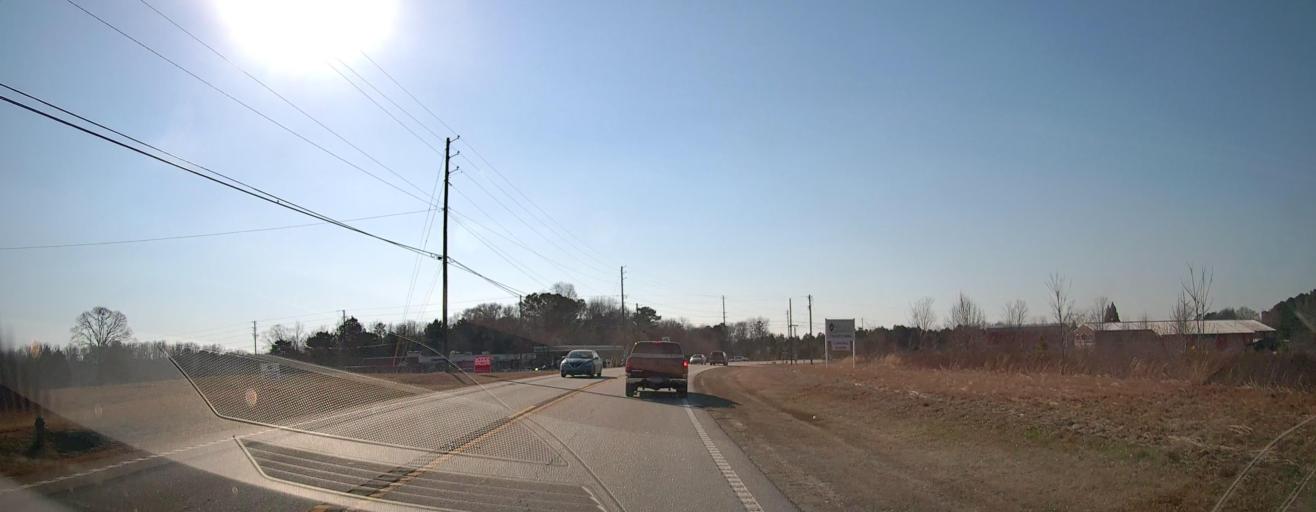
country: US
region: Georgia
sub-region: Henry County
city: Locust Grove
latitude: 33.3196
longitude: -84.0525
